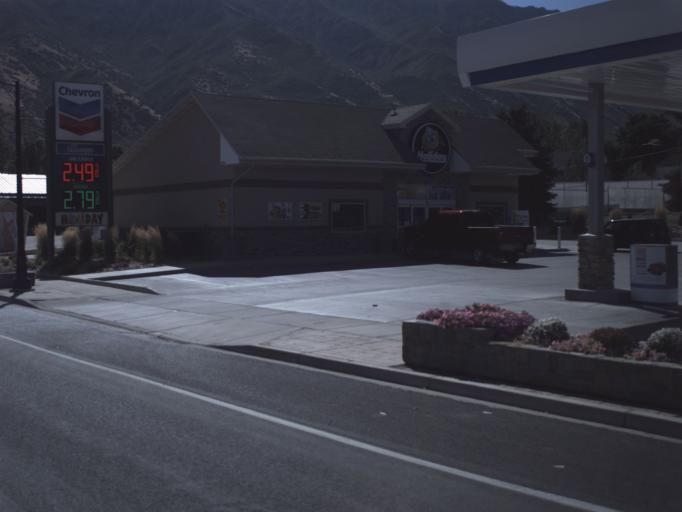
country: US
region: Utah
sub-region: Utah County
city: Santaquin
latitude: 39.9756
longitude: -111.7788
